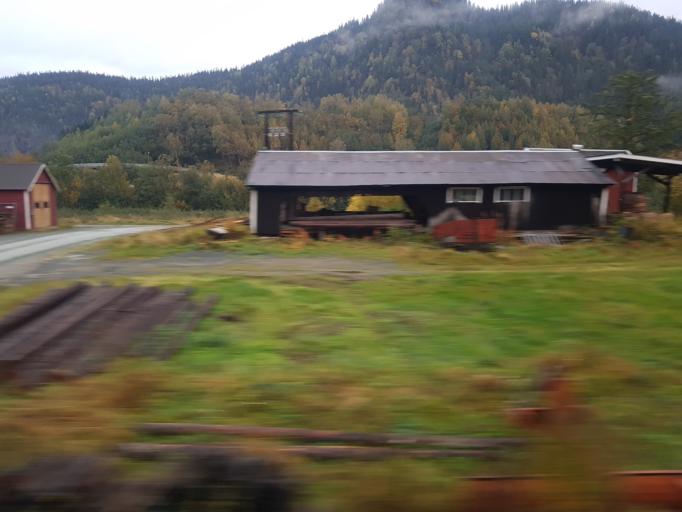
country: NO
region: Sor-Trondelag
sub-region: Midtre Gauldal
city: Storen
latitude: 63.0707
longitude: 10.2722
